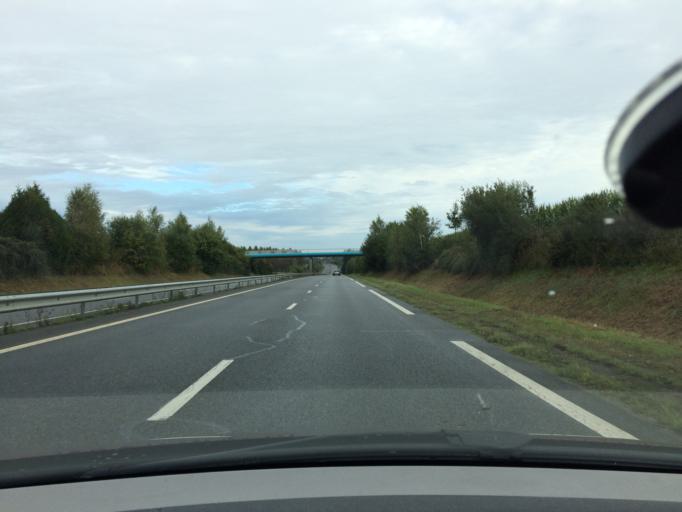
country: FR
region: Brittany
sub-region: Departement d'Ille-et-Vilaine
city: Saint-Armel
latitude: 48.0223
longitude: -1.6007
